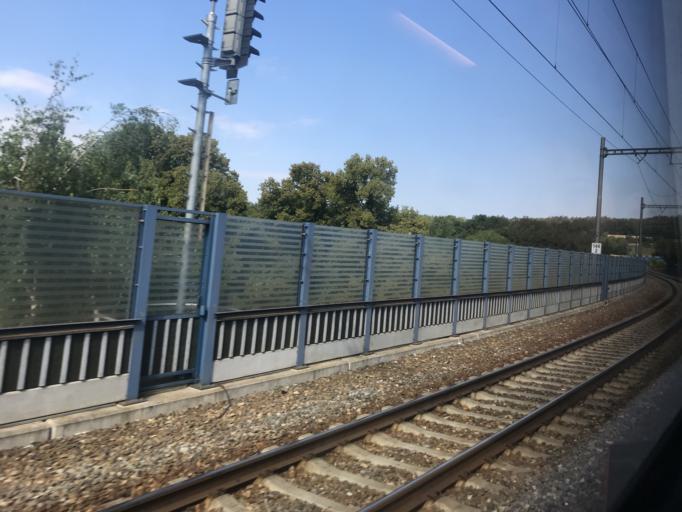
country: CZ
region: Central Bohemia
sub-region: Okres Benesov
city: Cercany
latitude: 49.8540
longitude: 14.7007
